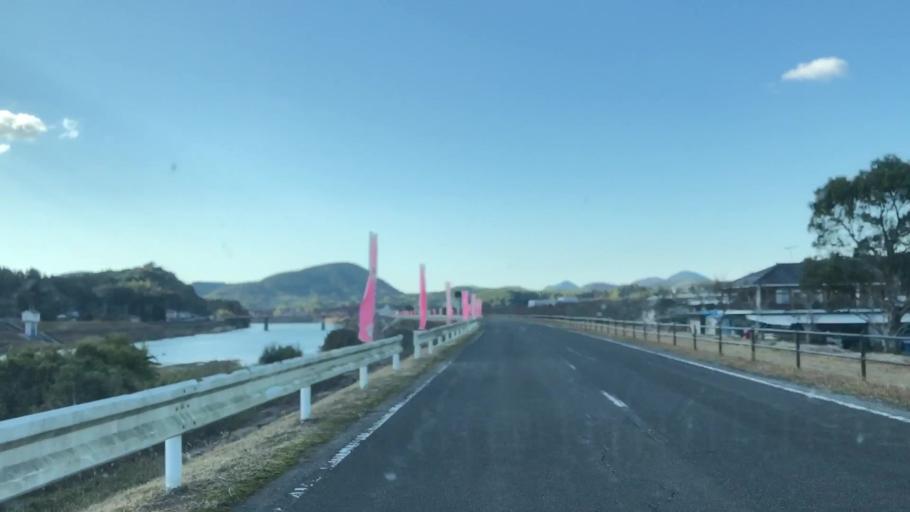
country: JP
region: Kagoshima
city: Satsumasendai
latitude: 31.8601
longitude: 130.3446
